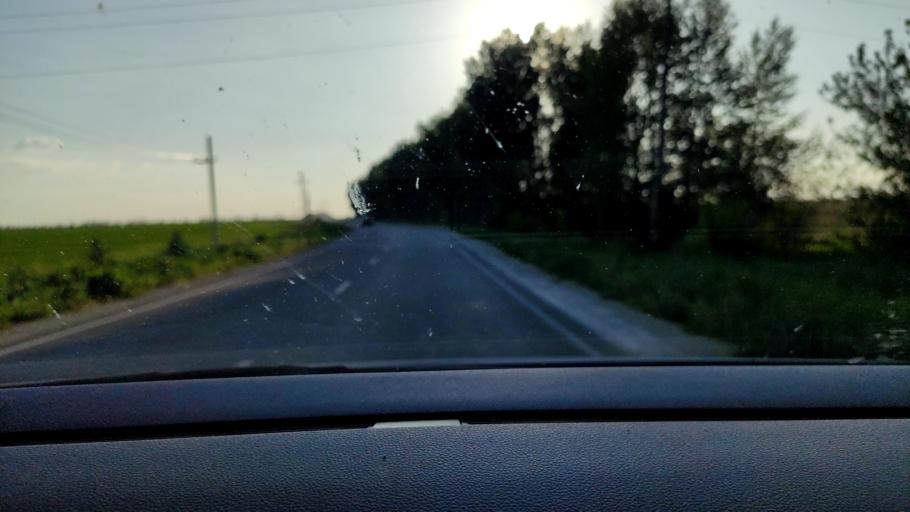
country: RU
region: Voronezj
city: Podkletnoye
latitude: 51.5058
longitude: 39.5213
